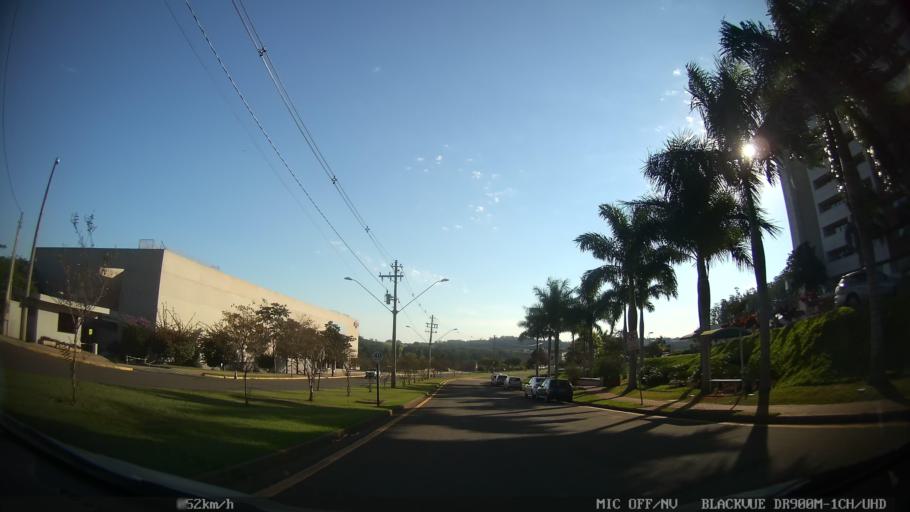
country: BR
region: Sao Paulo
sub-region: Piracicaba
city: Piracicaba
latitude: -22.6953
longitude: -47.6204
